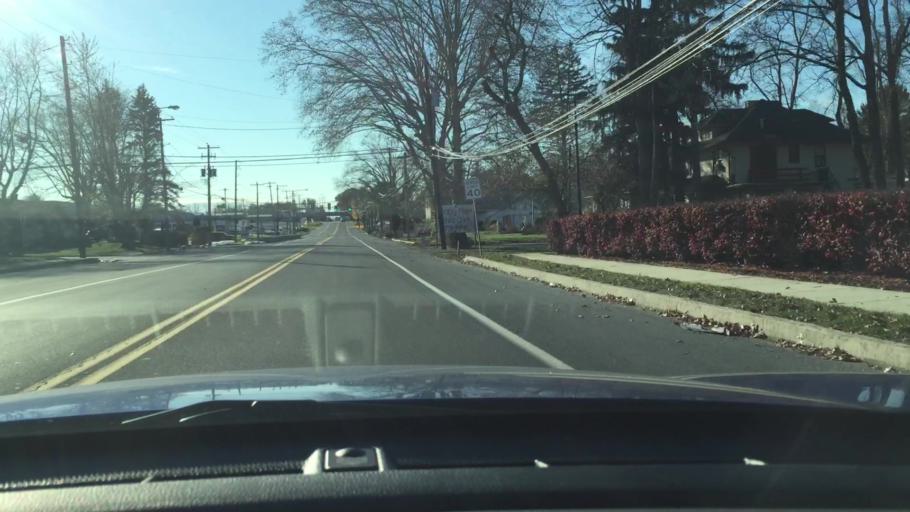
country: US
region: Pennsylvania
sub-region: Cumberland County
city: Shiremanstown
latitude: 40.2355
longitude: -76.9431
